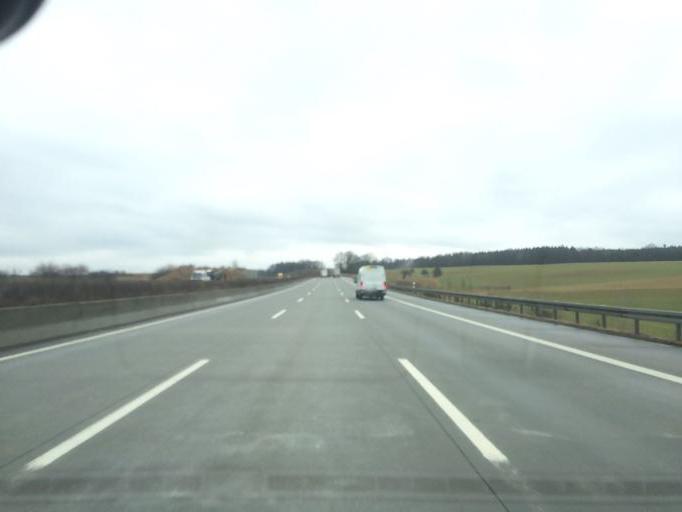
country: DE
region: Thuringia
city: Geroda
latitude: 50.7805
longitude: 11.8870
